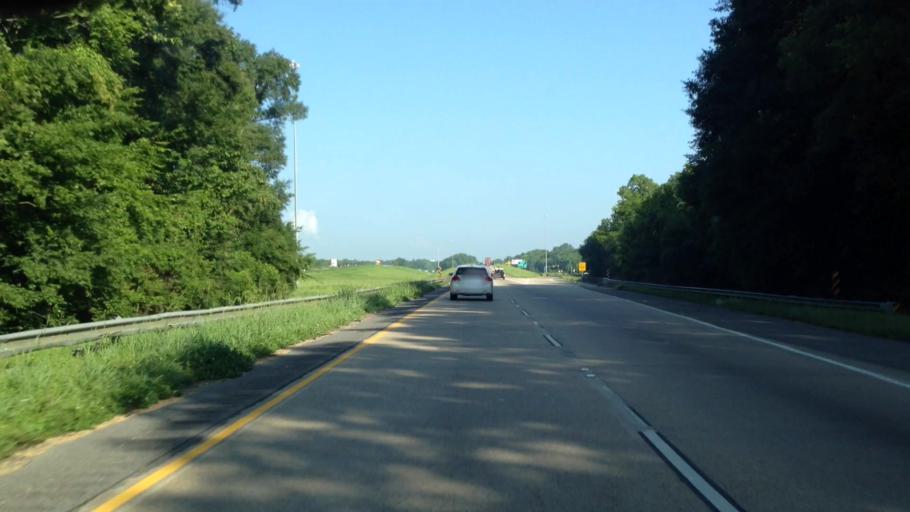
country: US
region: Louisiana
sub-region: Ascension Parish
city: Gonzales
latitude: 30.1898
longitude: -90.9142
